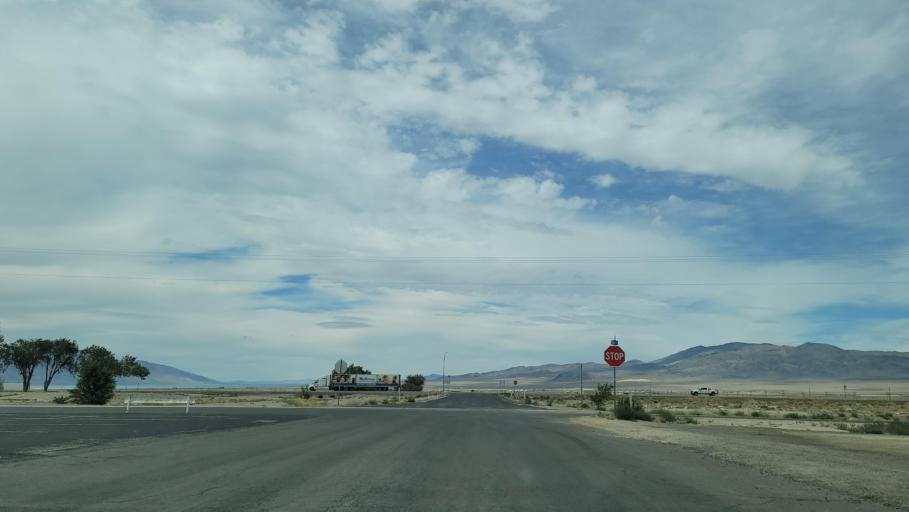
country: US
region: Nevada
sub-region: Mineral County
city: Hawthorne
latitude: 38.5320
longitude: -118.6189
